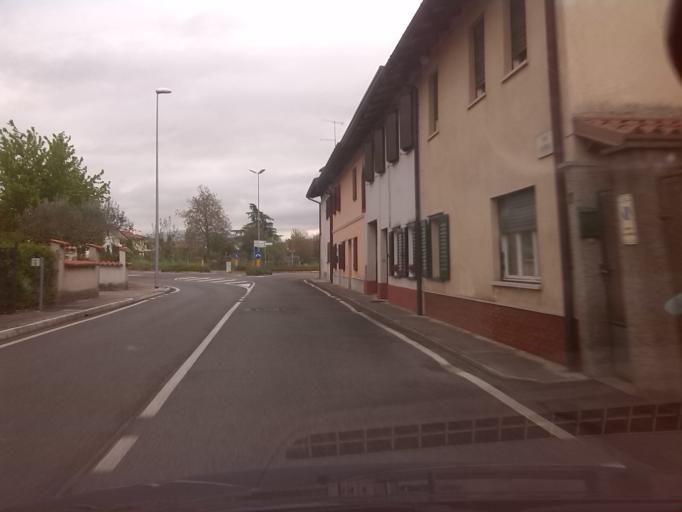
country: IT
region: Friuli Venezia Giulia
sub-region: Provincia di Gorizia
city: San Lorenzo Isontino
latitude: 45.9266
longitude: 13.5238
